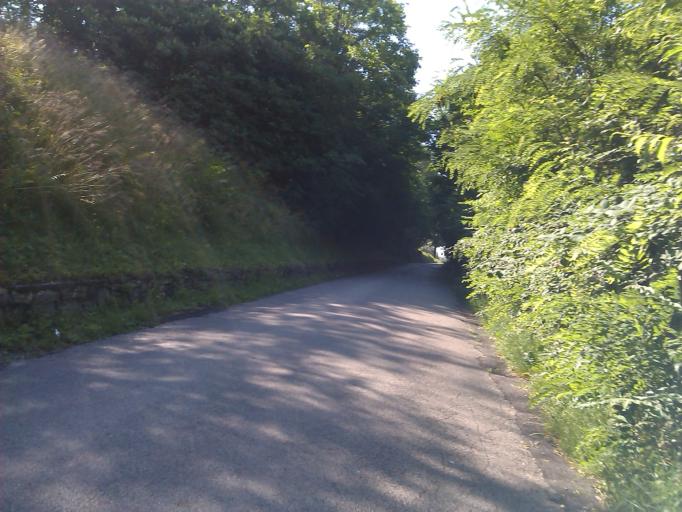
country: IT
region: Veneto
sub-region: Provincia di Vicenza
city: Bassano del Grappa
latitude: 45.7802
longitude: 11.7407
